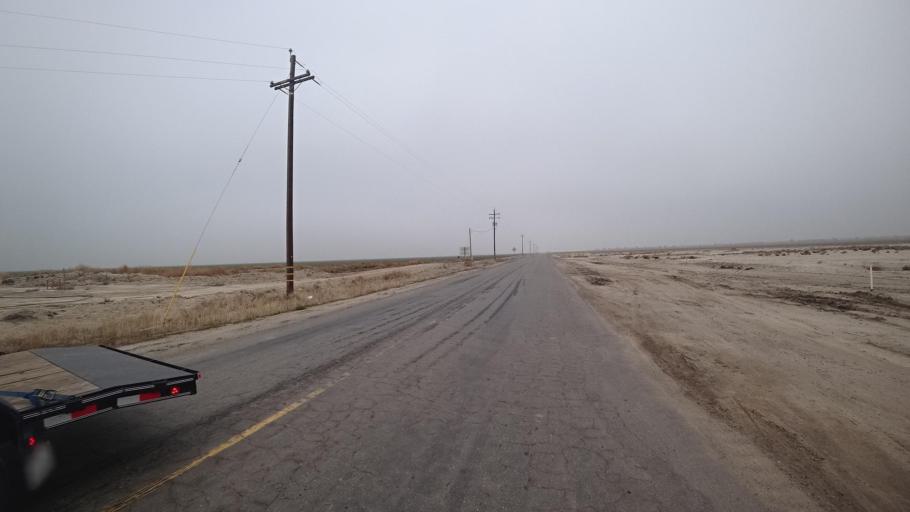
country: US
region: California
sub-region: Kern County
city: Rosedale
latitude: 35.2383
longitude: -119.2528
